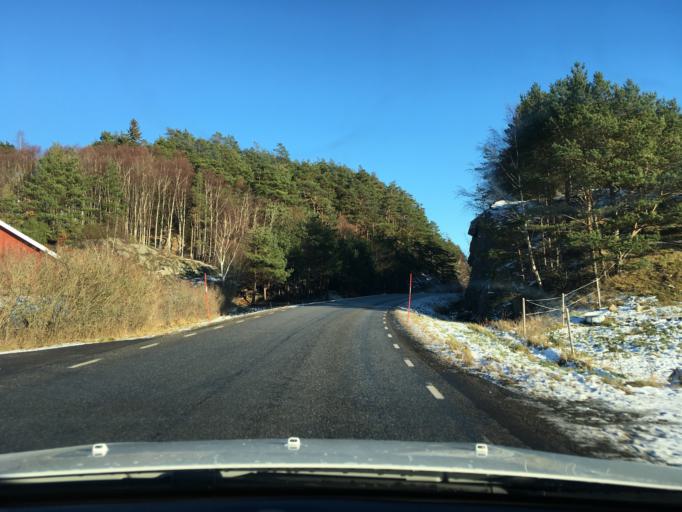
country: SE
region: Vaestra Goetaland
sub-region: Tjorns Kommun
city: Myggenas
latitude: 58.0347
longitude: 11.6625
